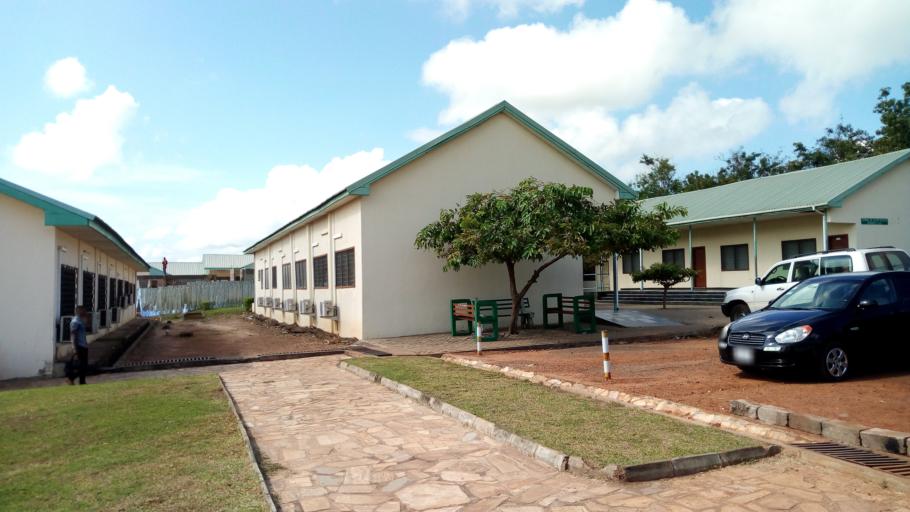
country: GH
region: Volta
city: Ho
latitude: 6.6018
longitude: 0.4856
